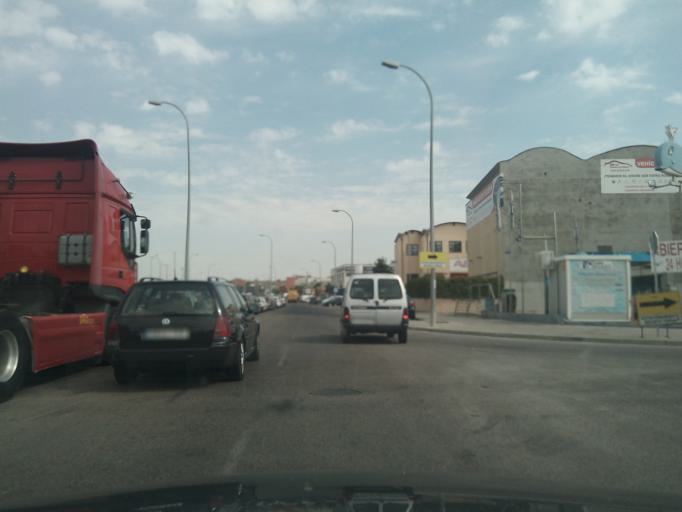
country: ES
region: Madrid
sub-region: Provincia de Madrid
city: Torrejon de Ardoz
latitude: 40.4490
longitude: -3.4822
